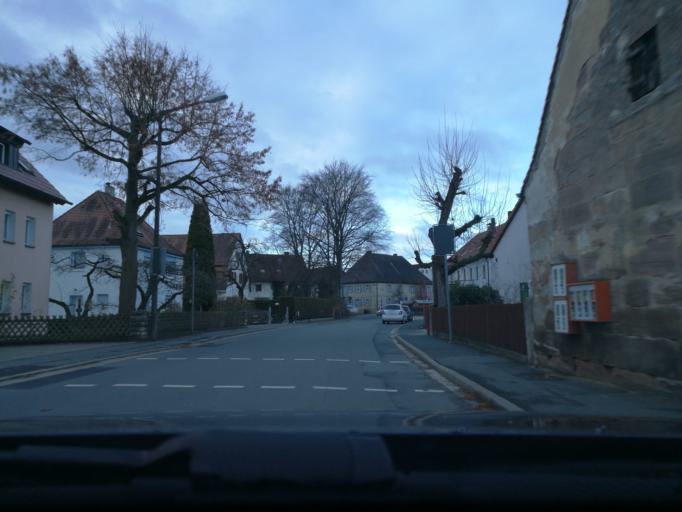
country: DE
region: Bavaria
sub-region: Regierungsbezirk Mittelfranken
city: Uttenreuth
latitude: 49.5992
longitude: 11.0755
